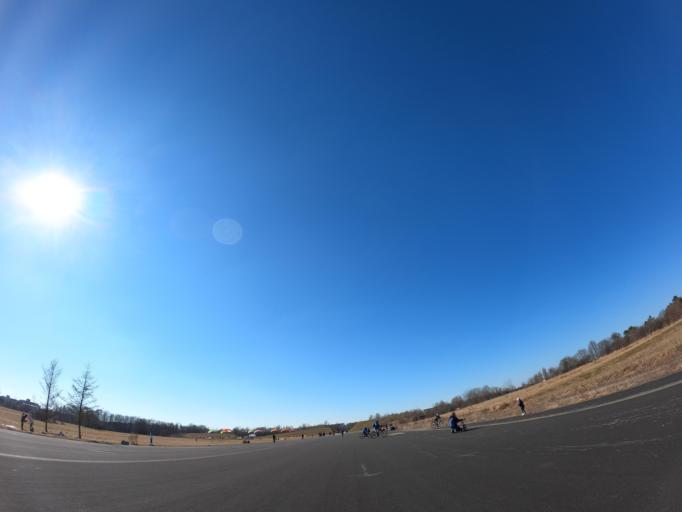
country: DE
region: Bavaria
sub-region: Upper Bavaria
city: Unterhaching
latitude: 48.0705
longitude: 11.6258
